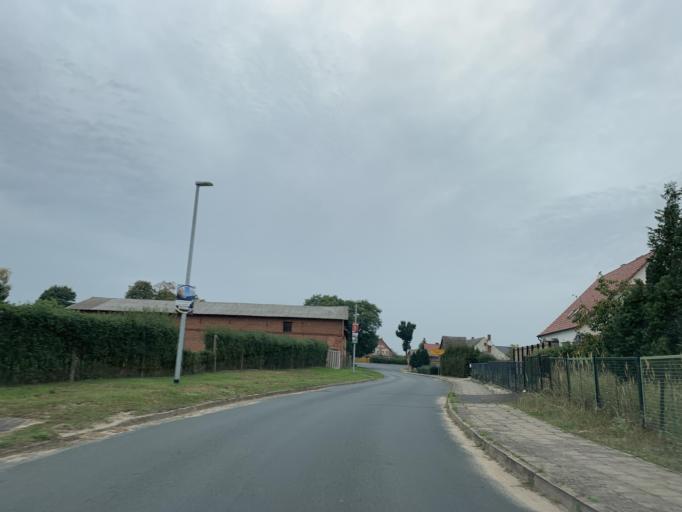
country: DE
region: Mecklenburg-Vorpommern
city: Woldegk
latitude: 53.3282
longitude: 13.5797
